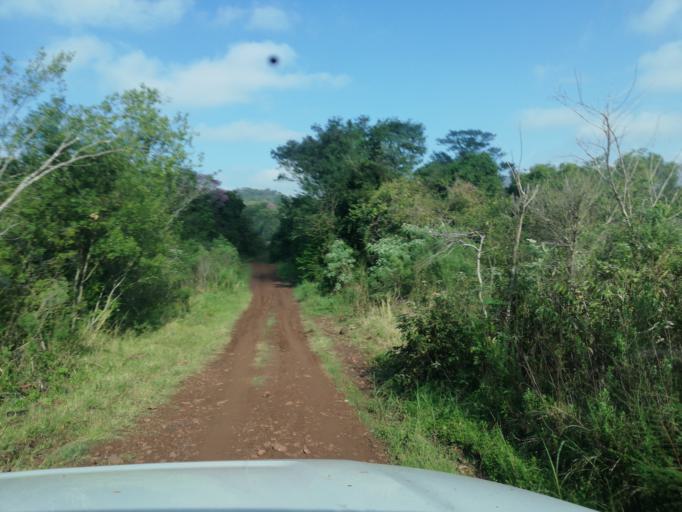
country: AR
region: Misiones
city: Cerro Azul
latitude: -27.6010
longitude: -55.5309
